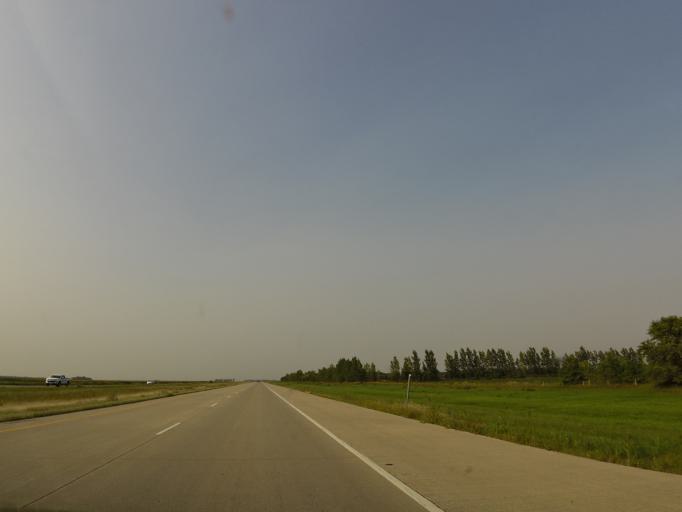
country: US
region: North Dakota
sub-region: Cass County
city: Horace
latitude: 46.5922
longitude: -96.8232
